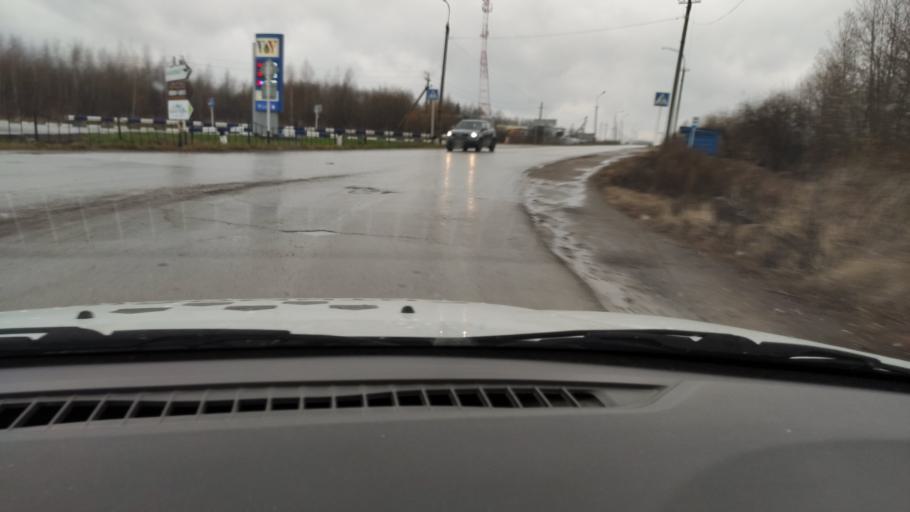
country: RU
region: Perm
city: Sylva
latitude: 58.0260
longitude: 56.7382
